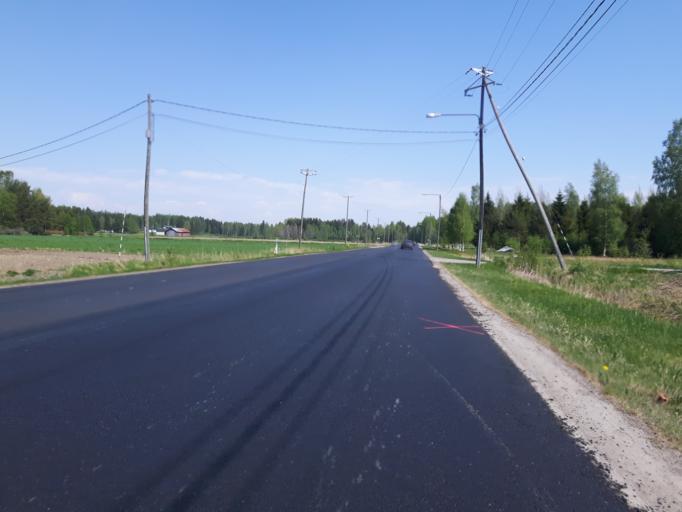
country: FI
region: Uusimaa
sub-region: Helsinki
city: Pornainen
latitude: 60.3322
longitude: 25.4502
